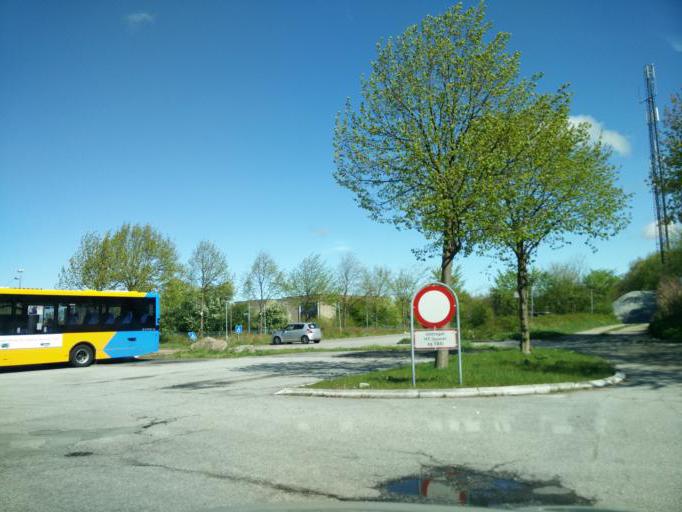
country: DK
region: Capital Region
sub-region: Gribskov Kommune
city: Helsinge
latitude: 56.0225
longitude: 12.2059
